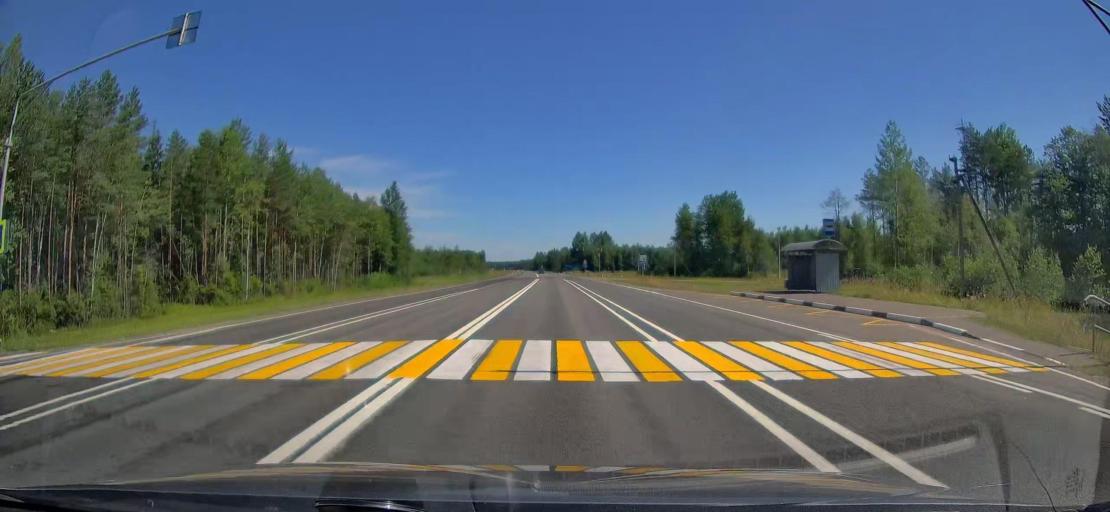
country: RU
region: Tverskaya
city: Ves'yegonsk
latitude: 58.9249
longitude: 37.2416
